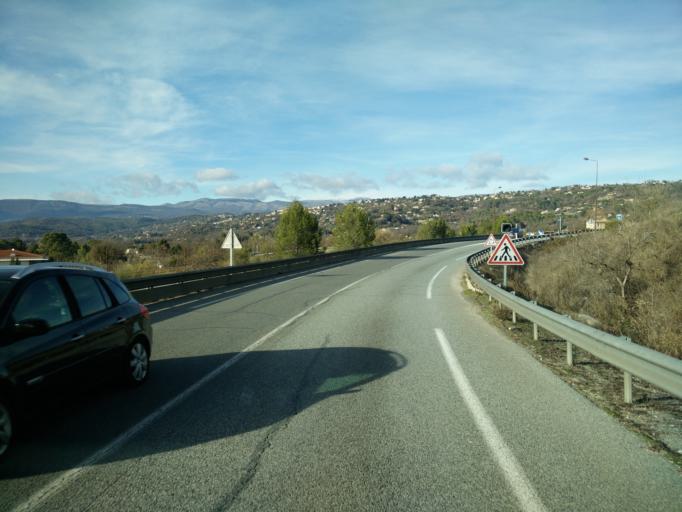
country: FR
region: Provence-Alpes-Cote d'Azur
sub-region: Departement du Var
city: Montauroux
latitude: 43.5977
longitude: 6.7864
